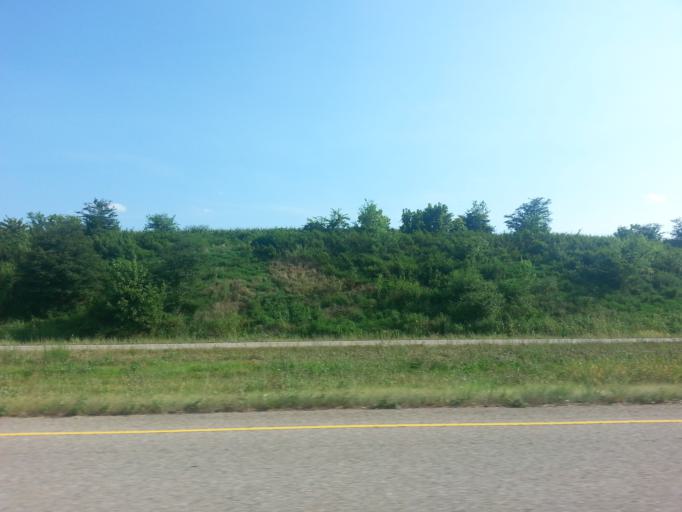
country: US
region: Tennessee
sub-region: Loudon County
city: Greenback
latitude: 35.7367
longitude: -84.1791
